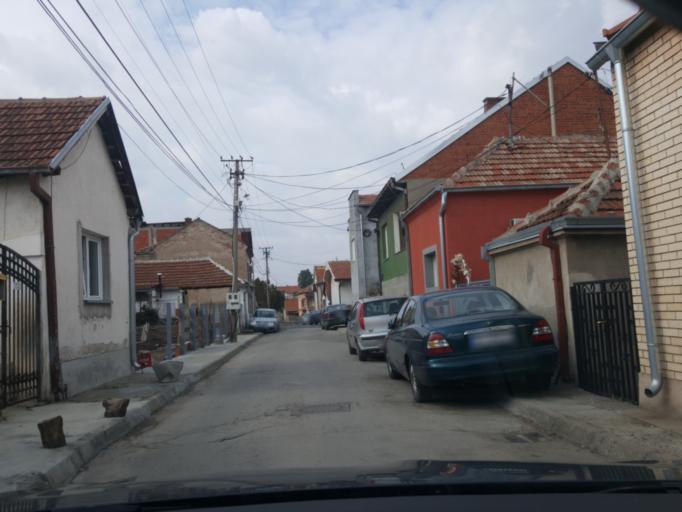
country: RS
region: Central Serbia
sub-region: Nisavski Okrug
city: Nis
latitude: 43.3132
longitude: 21.8772
